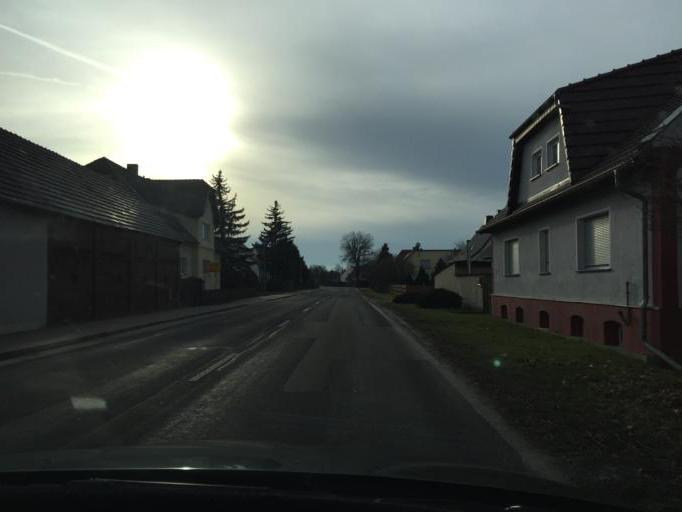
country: DE
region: Brandenburg
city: Peitz
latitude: 51.8663
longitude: 14.4174
